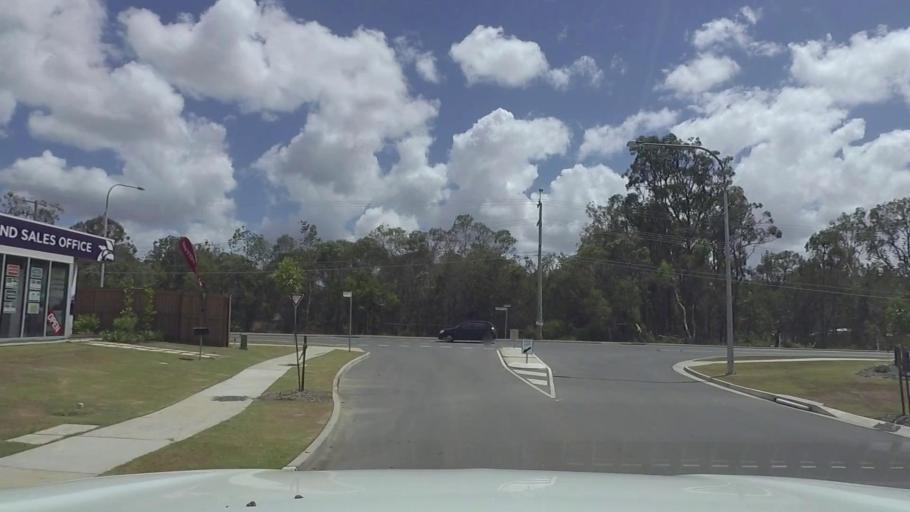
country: AU
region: Queensland
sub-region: Logan
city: Logan Reserve
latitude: -27.7070
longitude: 153.0793
